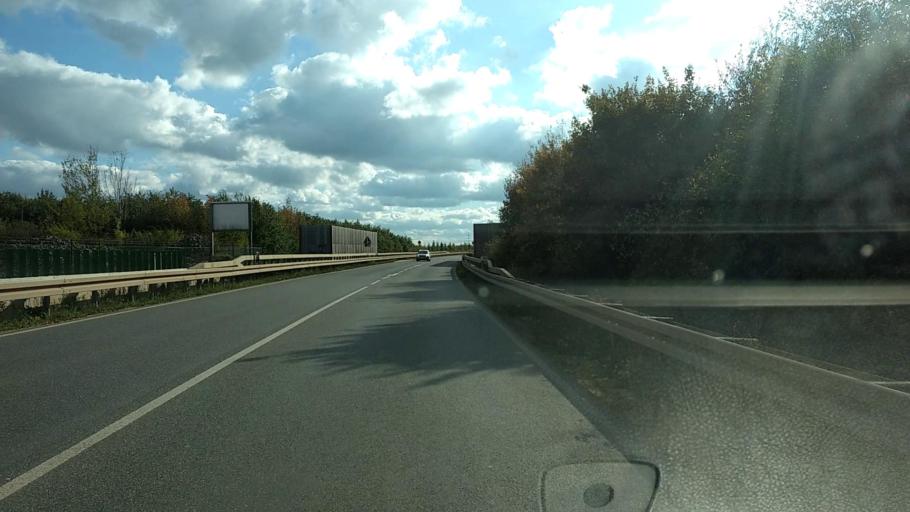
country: DE
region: North Rhine-Westphalia
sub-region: Regierungsbezirk Koln
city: Kerpen
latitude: 50.8839
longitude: 6.6436
